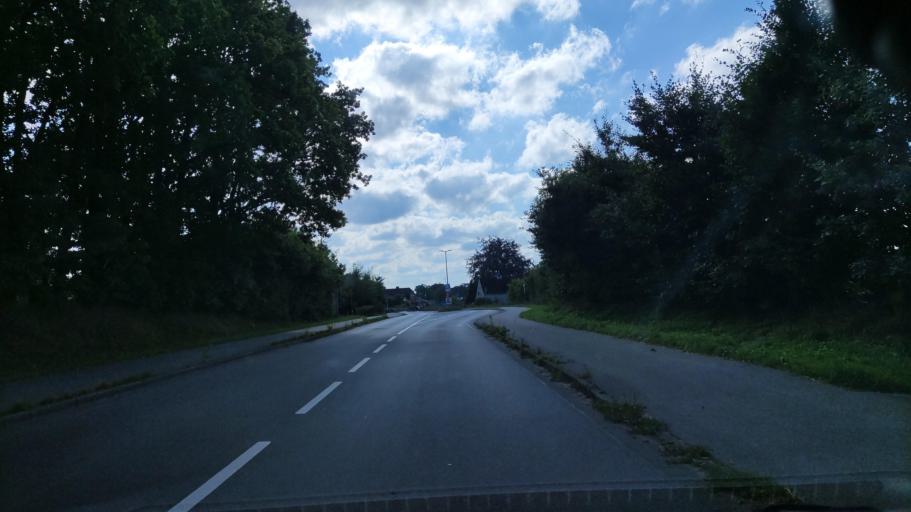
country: DE
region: Schleswig-Holstein
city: Alt Duvenstedt
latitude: 54.3650
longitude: 9.6516
